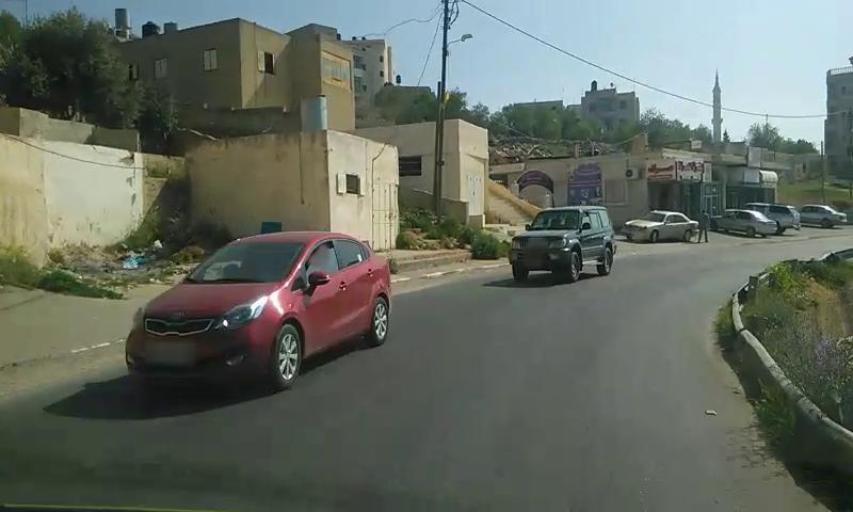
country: PS
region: West Bank
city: Dayr Jarir
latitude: 31.9706
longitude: 35.2869
